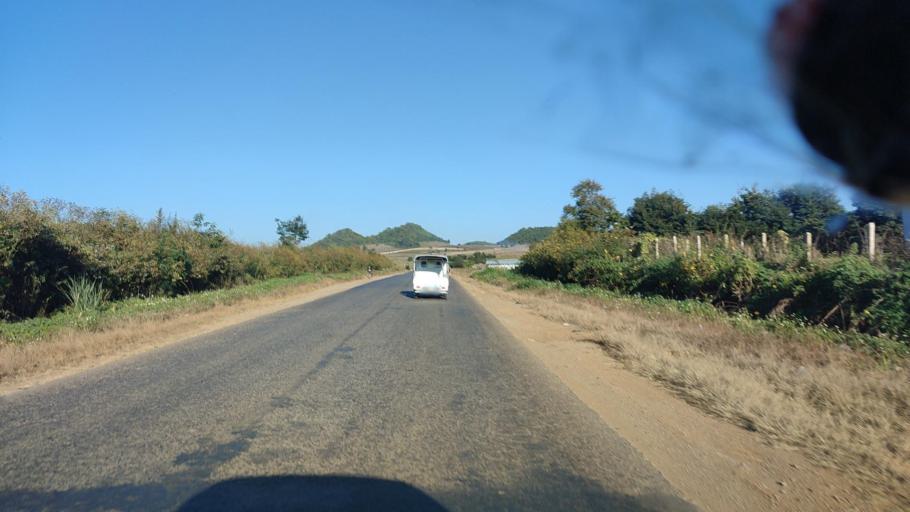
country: MM
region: Mandalay
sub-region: Pyin Oo Lwin District
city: Pyin Oo Lwin
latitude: 22.4442
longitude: 96.9626
